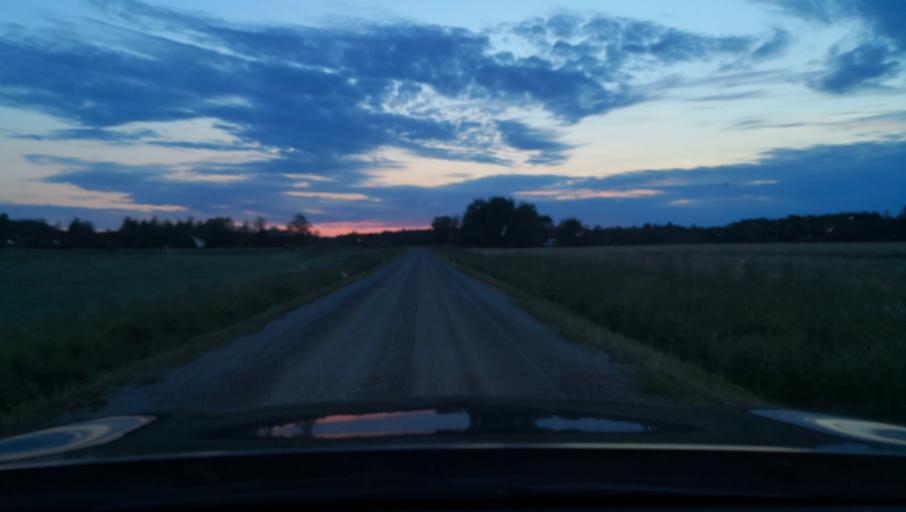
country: SE
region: Uppsala
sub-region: Heby Kommun
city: OEstervala
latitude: 60.0102
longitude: 17.3229
